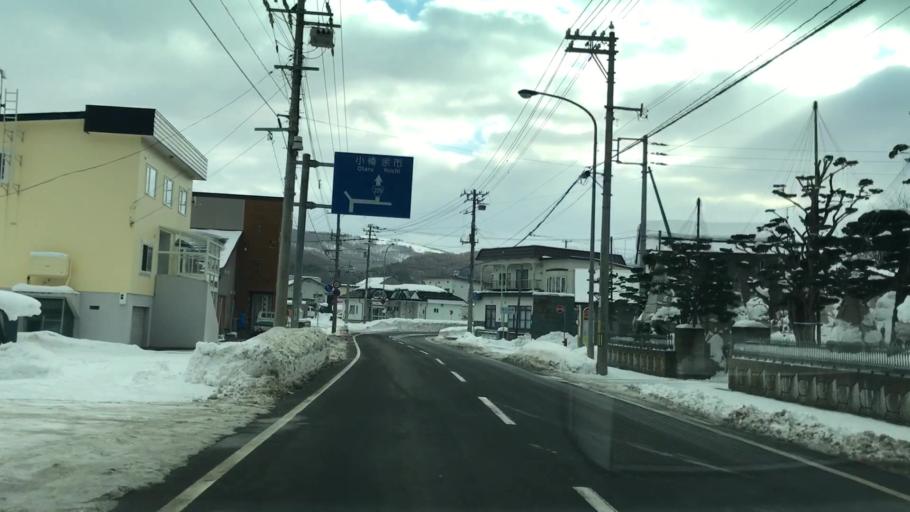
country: JP
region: Hokkaido
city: Yoichi
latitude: 43.2670
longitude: 140.6391
